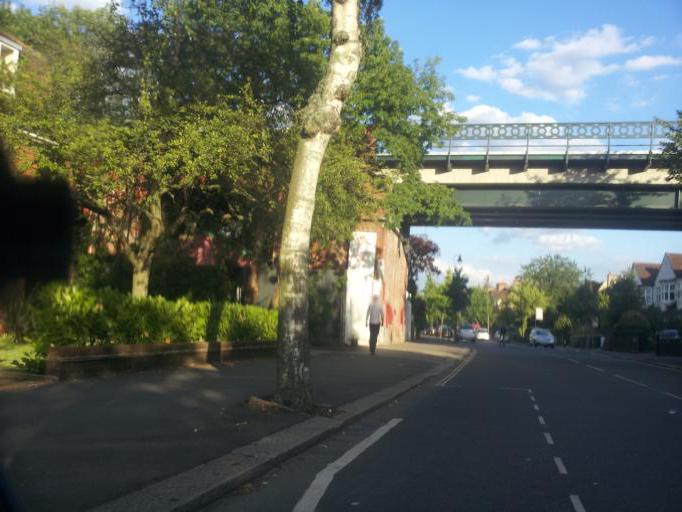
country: GB
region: England
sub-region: Greater London
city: Brixton
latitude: 51.4509
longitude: -0.0951
